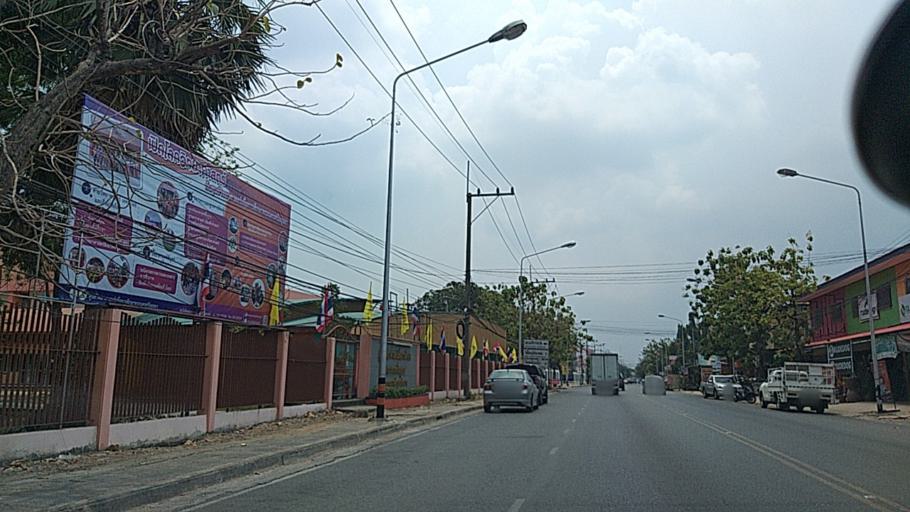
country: TH
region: Phra Nakhon Si Ayutthaya
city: Phra Nakhon Si Ayutthaya
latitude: 14.3526
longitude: 100.5982
